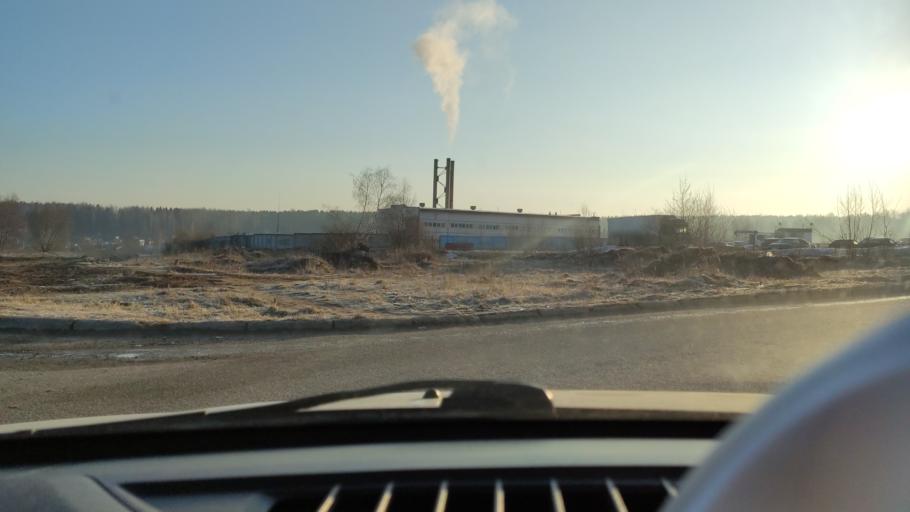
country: RU
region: Perm
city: Polazna
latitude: 58.1368
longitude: 56.3955
